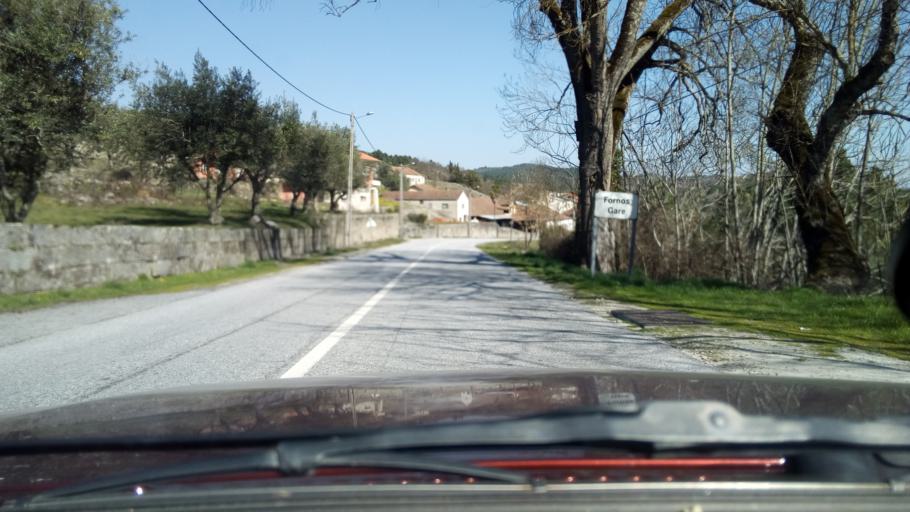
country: PT
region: Guarda
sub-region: Fornos de Algodres
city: Fornos de Algodres
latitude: 40.6111
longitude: -7.5284
